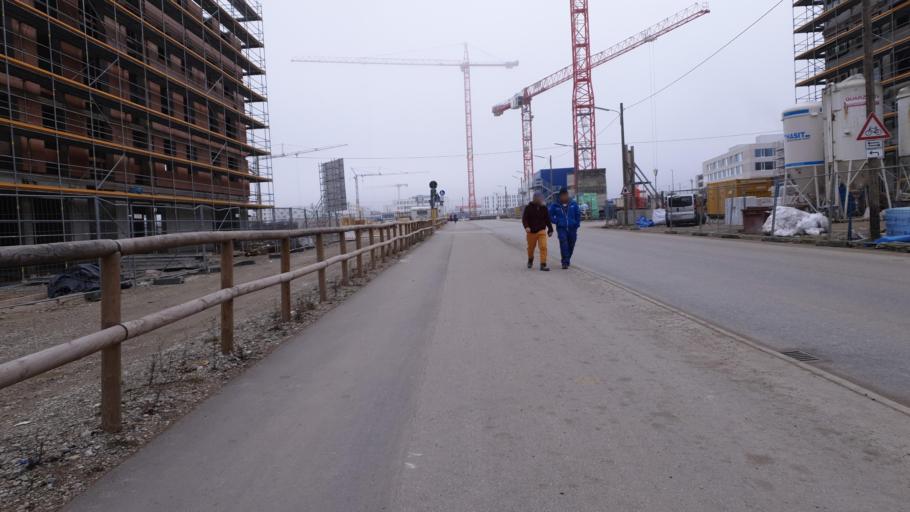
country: DE
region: Bavaria
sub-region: Upper Bavaria
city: Germering
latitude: 48.1443
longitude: 11.4071
